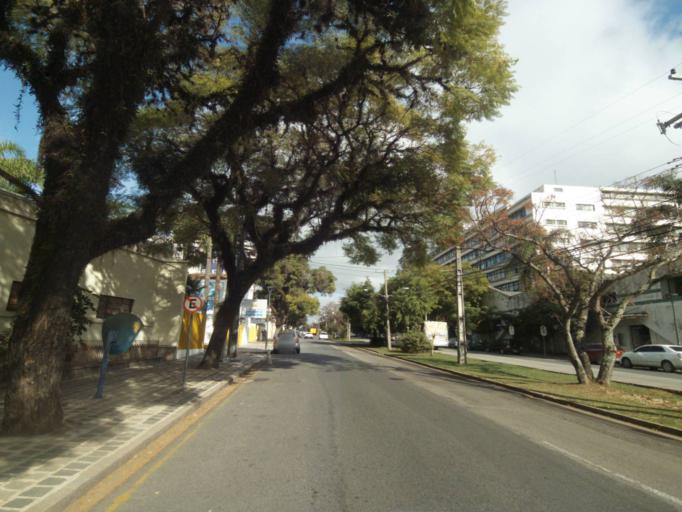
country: BR
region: Parana
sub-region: Curitiba
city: Curitiba
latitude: -25.4406
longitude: -49.2648
